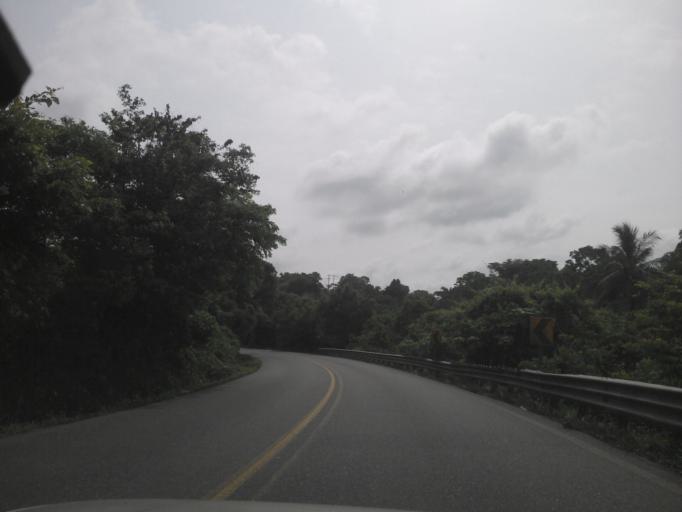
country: MX
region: Veracruz
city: Gutierrez Zamora
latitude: 20.4623
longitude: -97.1365
